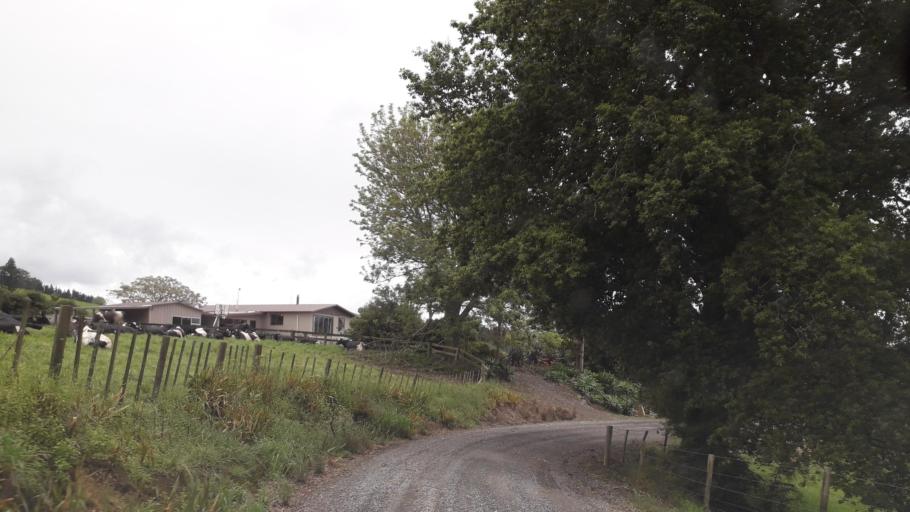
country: NZ
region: Northland
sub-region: Far North District
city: Waimate North
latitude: -35.3003
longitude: 173.5647
